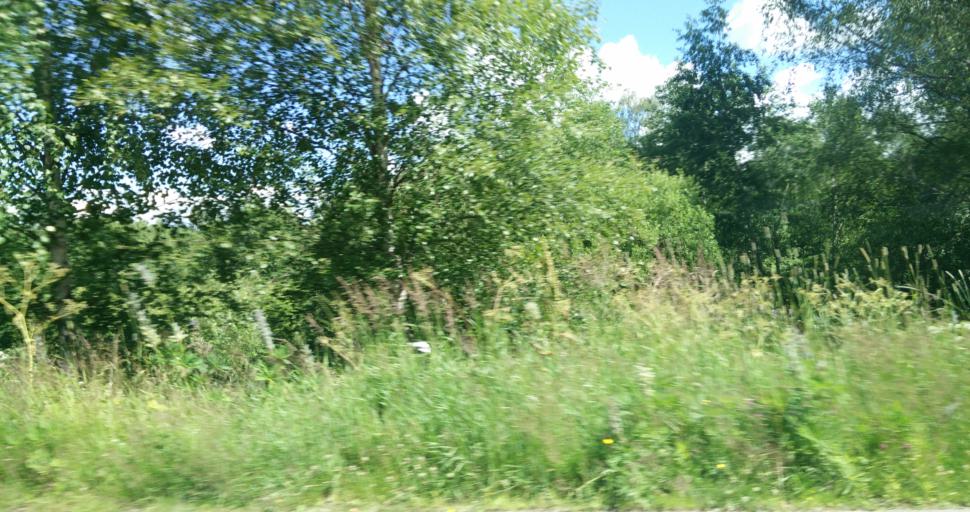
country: SE
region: Vaermland
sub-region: Hagfors Kommun
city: Hagfors
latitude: 60.0239
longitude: 13.6803
